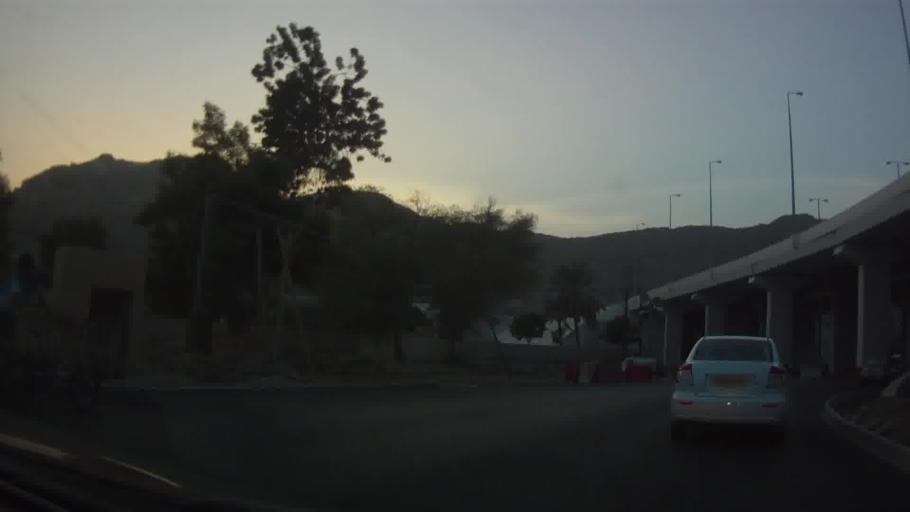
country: OM
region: Muhafazat Masqat
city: Muscat
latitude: 23.6191
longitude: 58.5405
